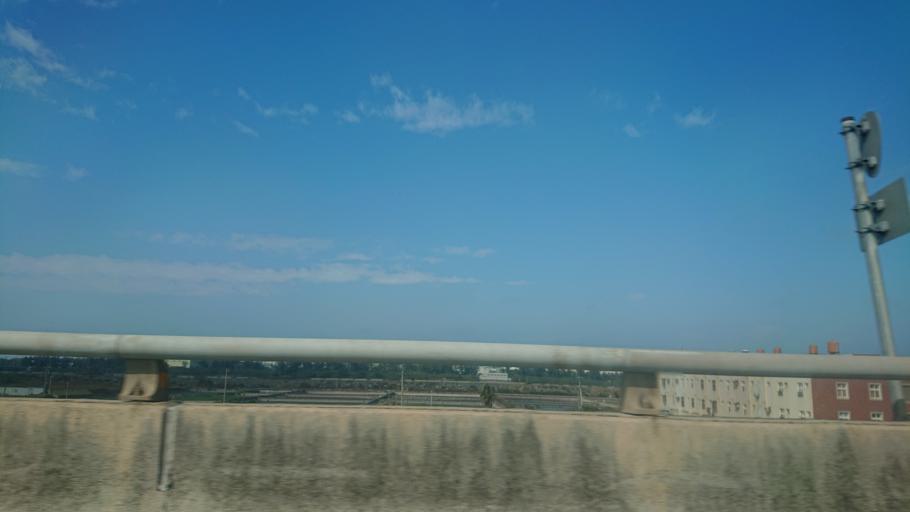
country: TW
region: Taiwan
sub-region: Changhua
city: Chang-hua
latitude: 24.0661
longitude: 120.4120
